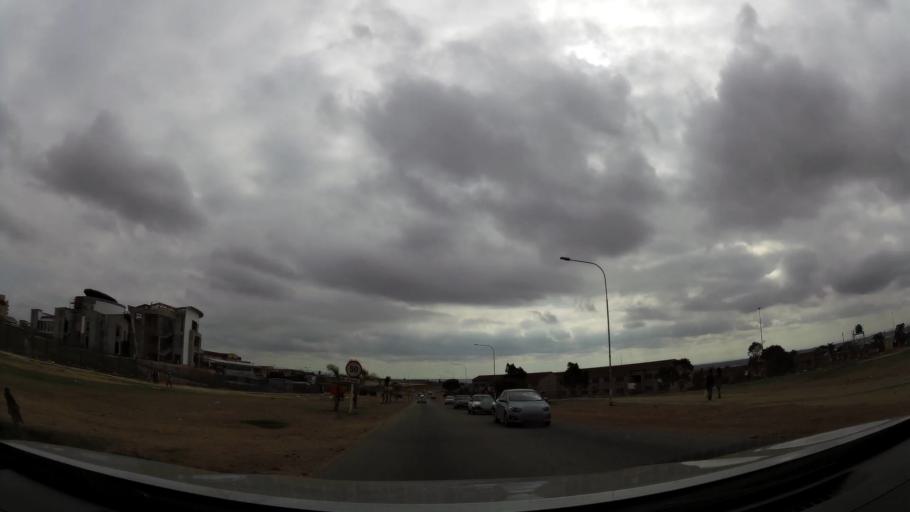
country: ZA
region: Eastern Cape
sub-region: Nelson Mandela Bay Metropolitan Municipality
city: Port Elizabeth
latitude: -33.8800
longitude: 25.5638
